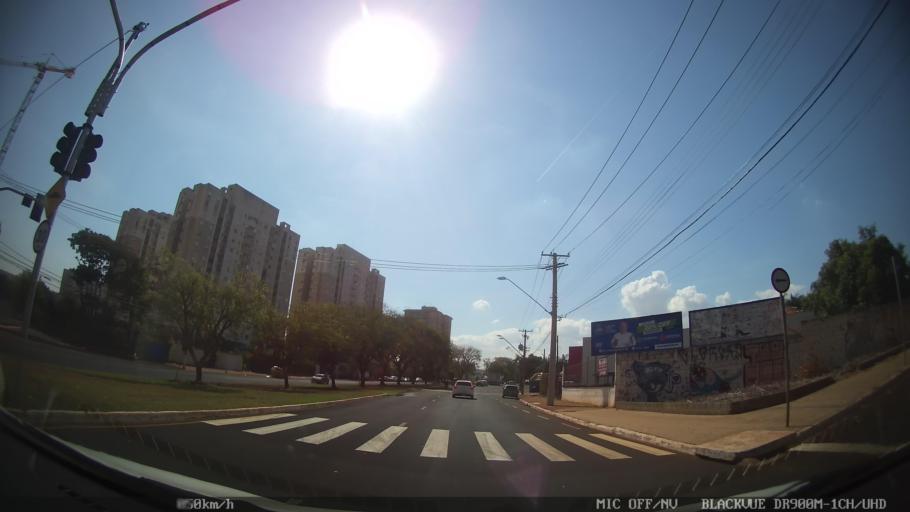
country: BR
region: Sao Paulo
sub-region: Ribeirao Preto
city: Ribeirao Preto
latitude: -21.1994
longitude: -47.8230
